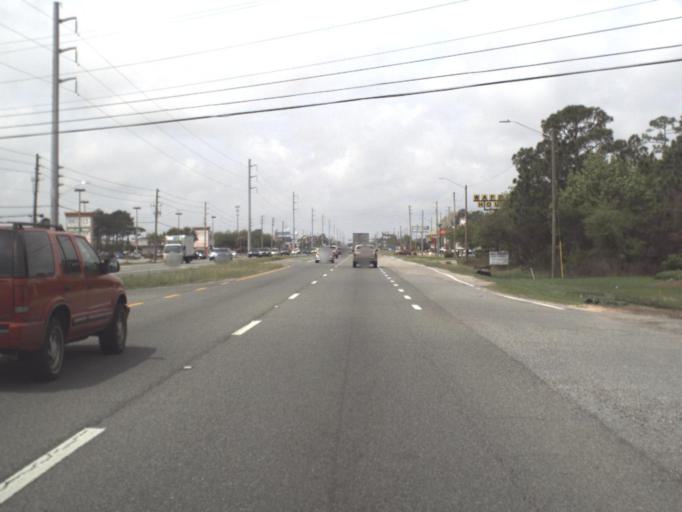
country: US
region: Florida
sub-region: Santa Rosa County
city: Oriole Beach
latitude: 30.3875
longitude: -87.0828
